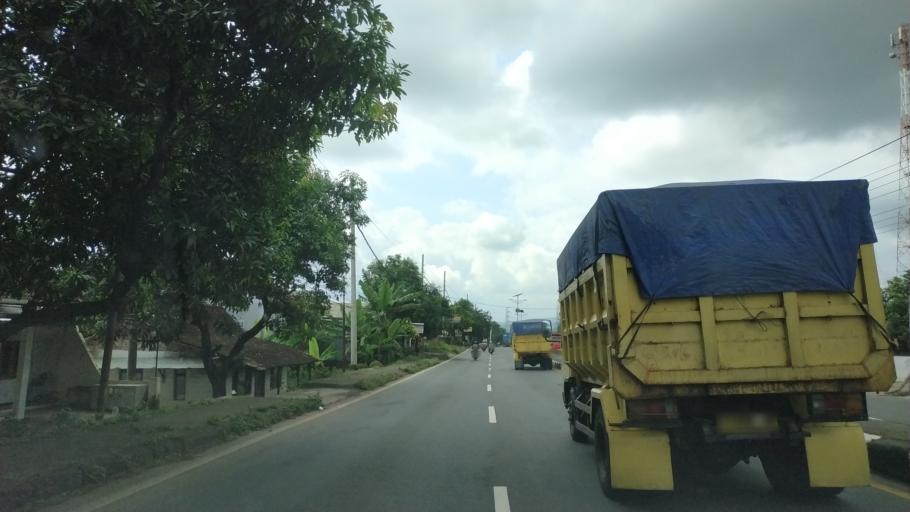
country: ID
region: Central Java
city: Pekalongan
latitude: -6.9485
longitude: 109.7866
